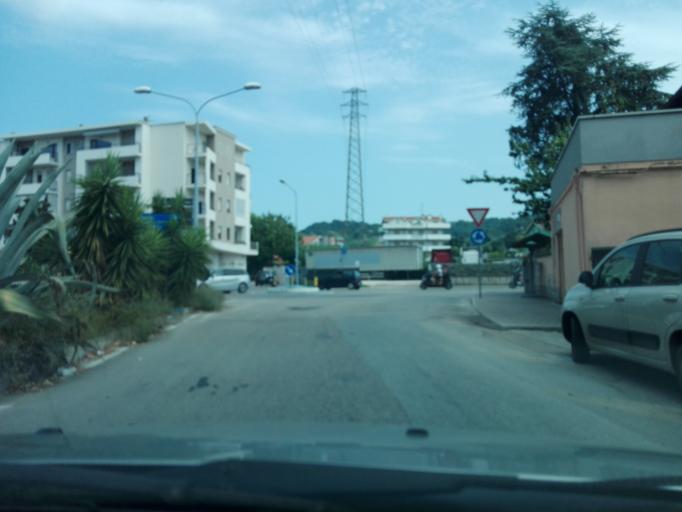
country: IT
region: Abruzzo
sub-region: Provincia di Pescara
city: Montesilvano Marina
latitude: 42.5032
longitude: 14.1349
